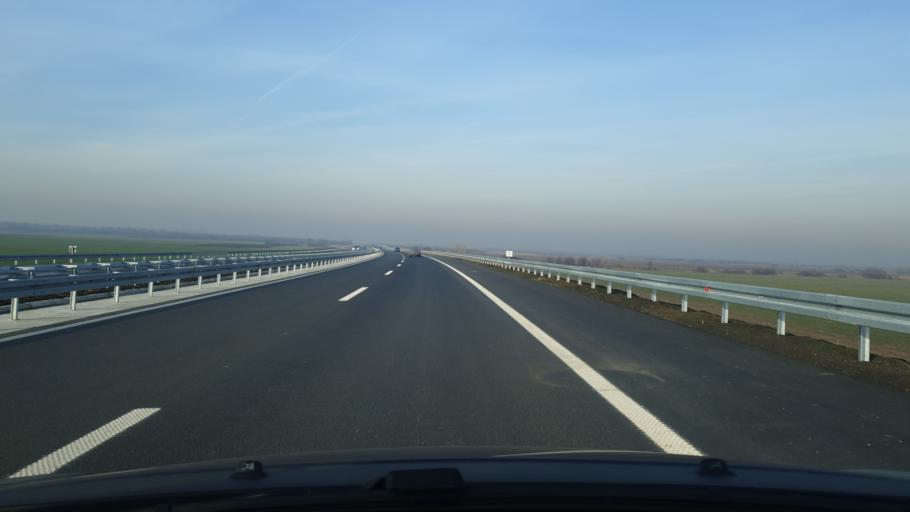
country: RS
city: Umka
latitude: 44.6918
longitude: 20.2674
